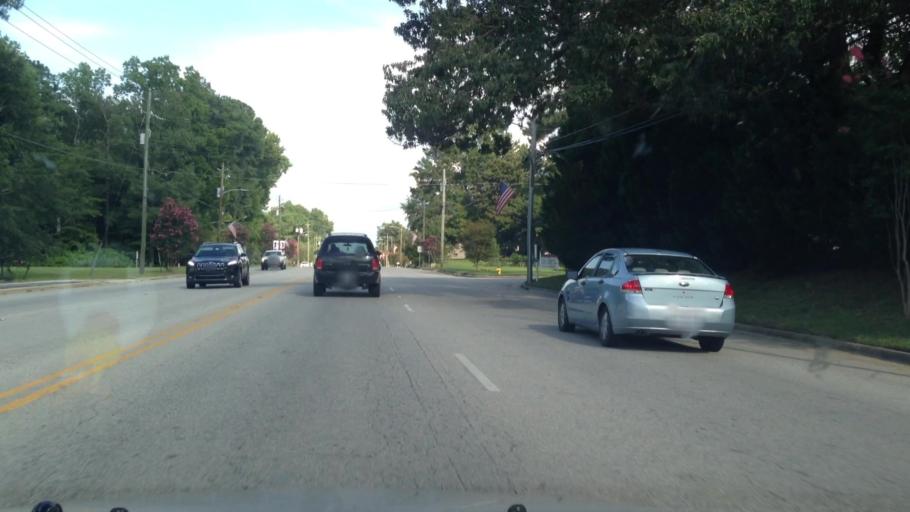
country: US
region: North Carolina
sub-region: Harnett County
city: Lillington
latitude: 35.4006
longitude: -78.8232
